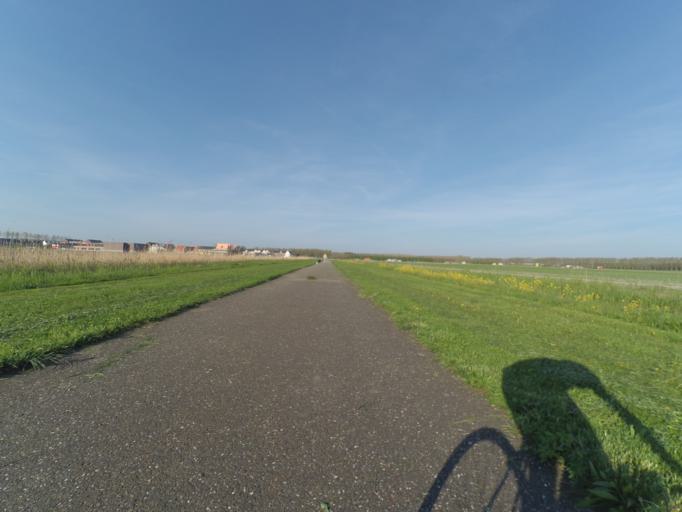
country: NL
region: Flevoland
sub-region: Gemeente Almere
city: Almere Stad
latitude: 52.3620
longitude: 5.2869
